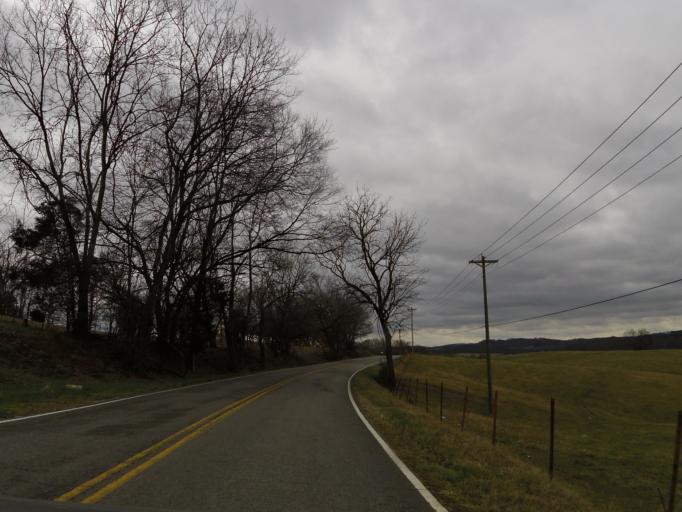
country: US
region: Tennessee
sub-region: Jefferson County
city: Jefferson City
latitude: 36.1869
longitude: -83.5365
